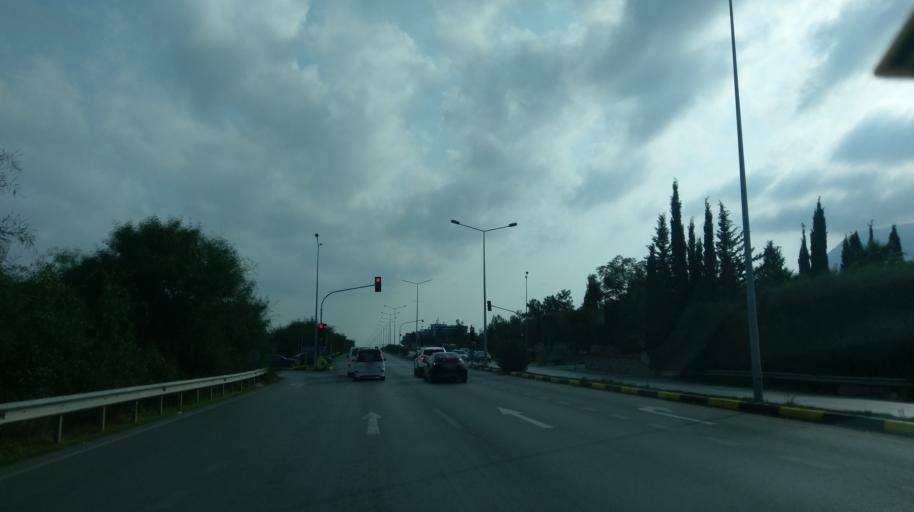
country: CY
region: Keryneia
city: Kyrenia
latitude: 35.3283
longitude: 33.2969
